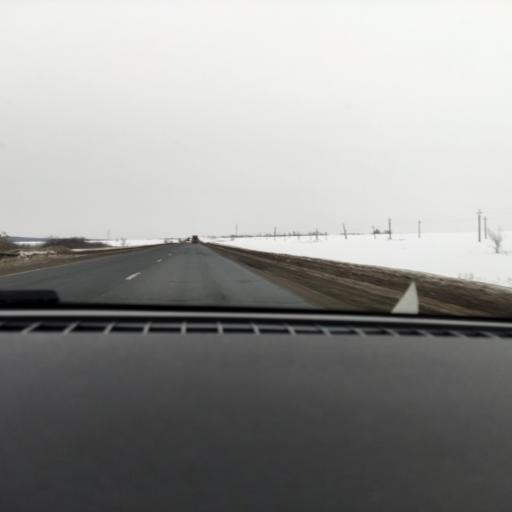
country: RU
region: Samara
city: Smyshlyayevka
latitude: 53.2881
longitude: 50.4608
